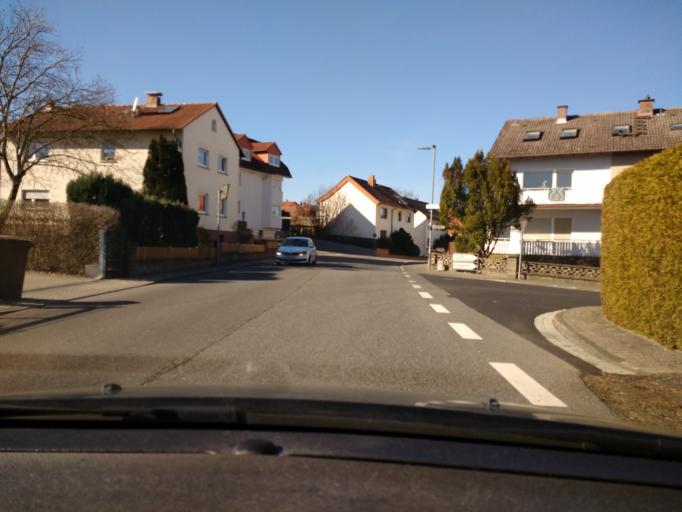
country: DE
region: Hesse
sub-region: Regierungsbezirk Darmstadt
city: Rodenbach
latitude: 50.1342
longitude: 9.0640
